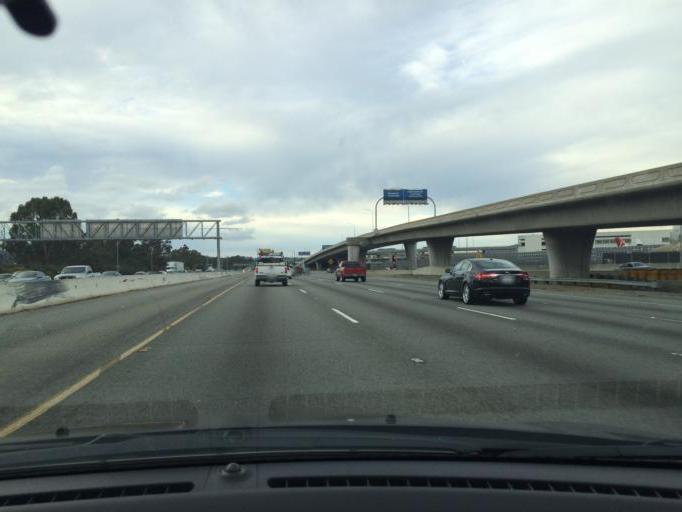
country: US
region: California
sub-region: San Mateo County
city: Millbrae
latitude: 37.6085
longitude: -122.3894
